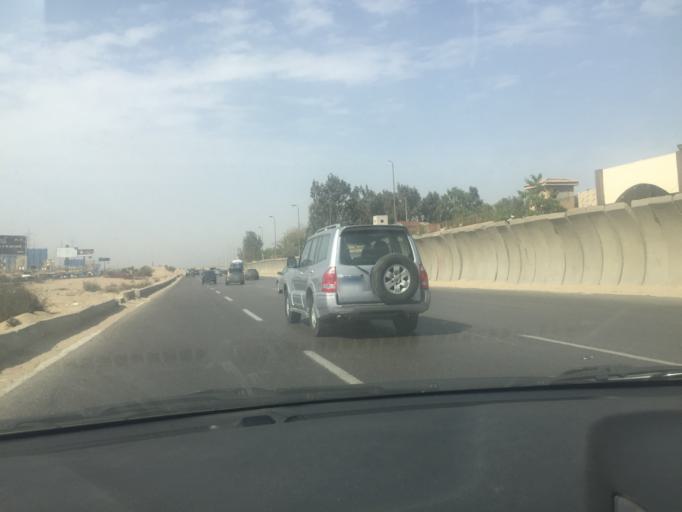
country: EG
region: Muhafazat al Qalyubiyah
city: Al Khankah
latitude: 30.0825
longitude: 31.4620
